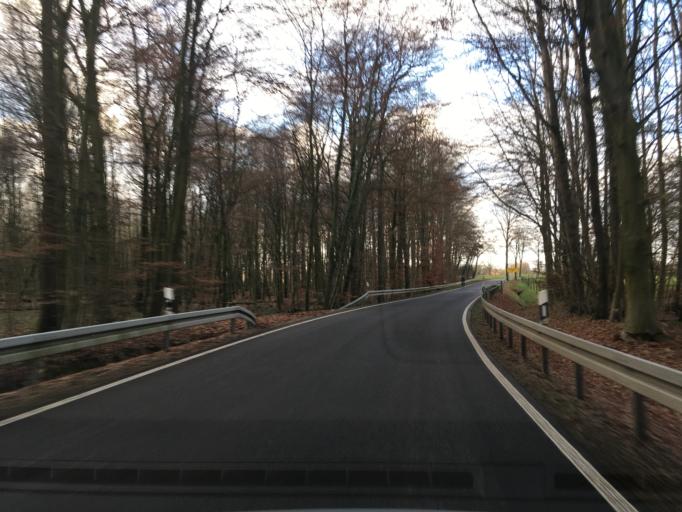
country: DE
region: North Rhine-Westphalia
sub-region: Regierungsbezirk Munster
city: Gescher
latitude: 51.9580
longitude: 7.0274
